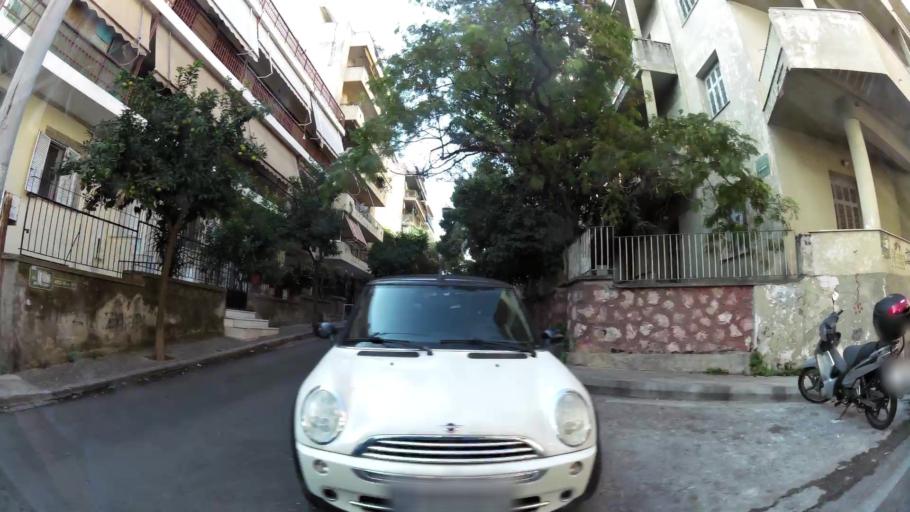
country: GR
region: Attica
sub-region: Nomarchia Athinas
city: Kaisariani
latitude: 37.9754
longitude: 23.7706
